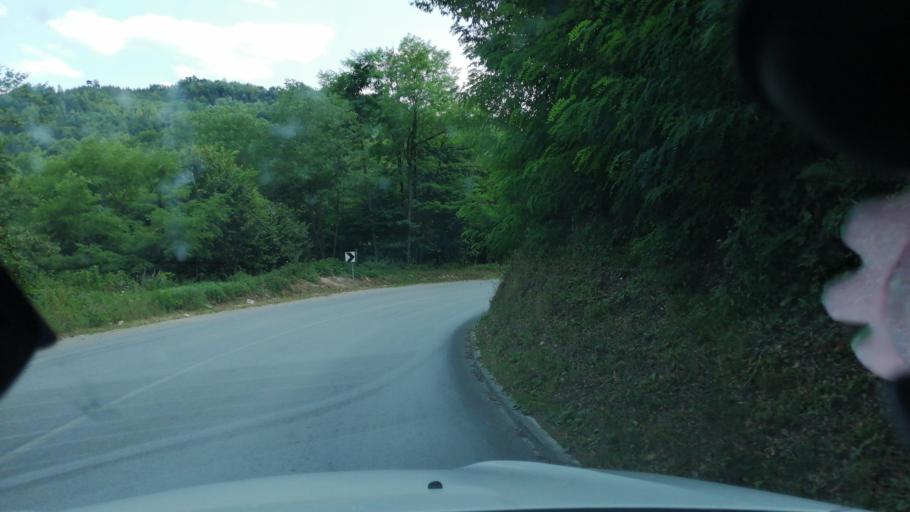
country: RS
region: Central Serbia
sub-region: Moravicki Okrug
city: Ivanjica
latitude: 43.6166
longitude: 20.2367
